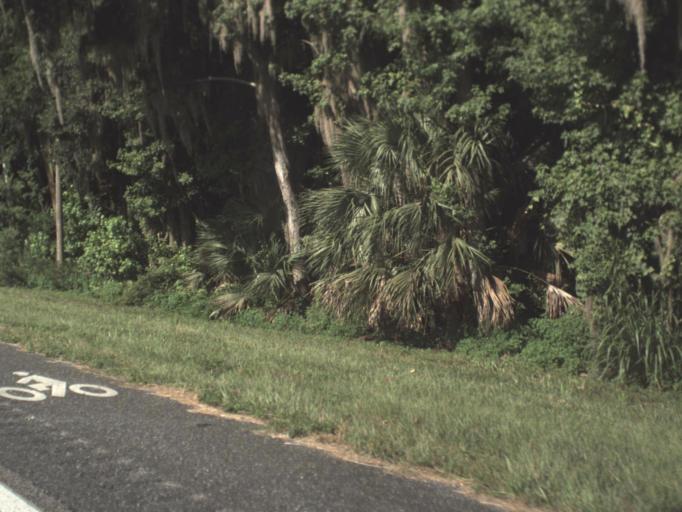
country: US
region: Florida
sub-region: Alachua County
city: Gainesville
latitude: 29.5338
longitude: -82.3089
